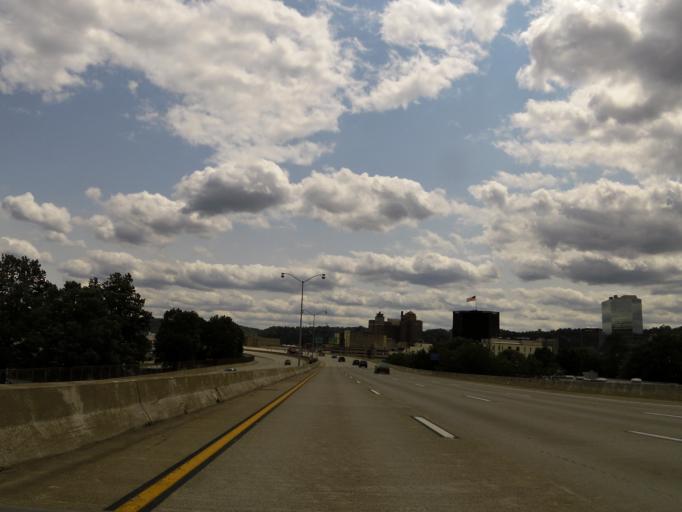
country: US
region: West Virginia
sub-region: Kanawha County
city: Charleston
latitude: 38.3575
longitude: -81.6320
